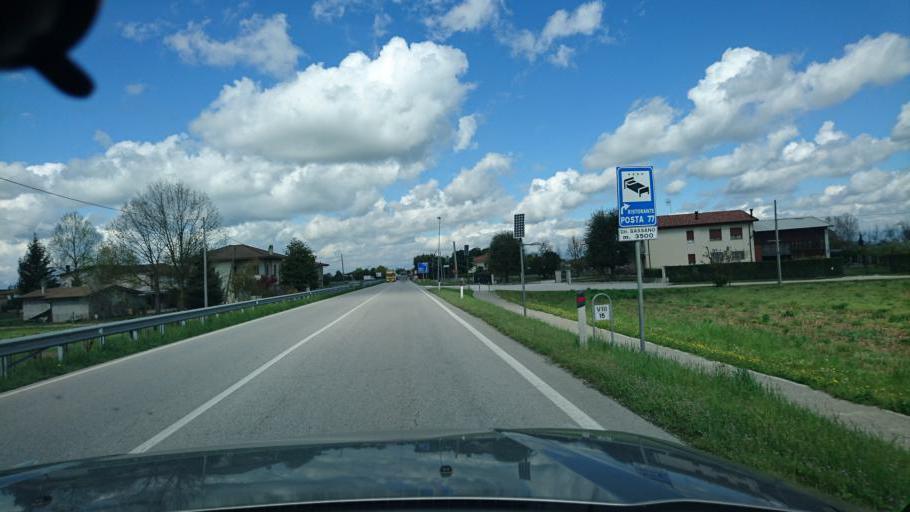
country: IT
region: Veneto
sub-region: Provincia di Padova
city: Tremignon
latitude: 45.5257
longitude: 11.7965
